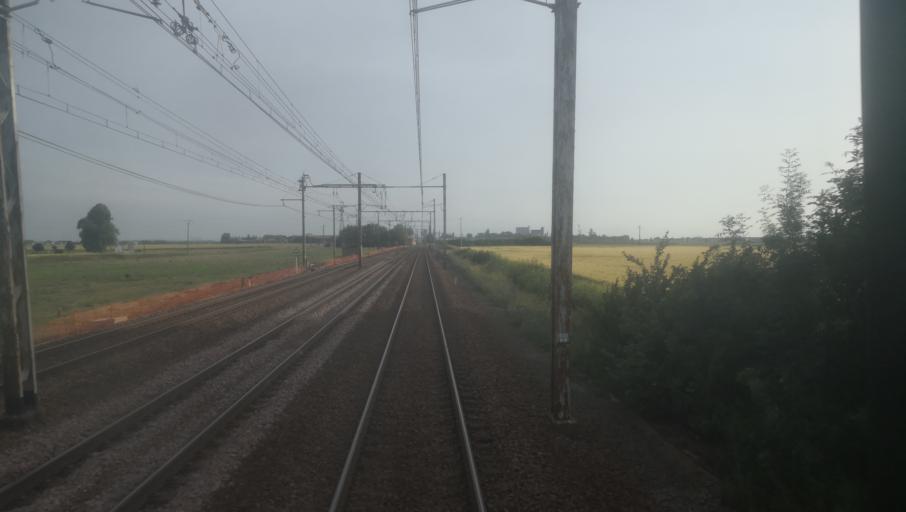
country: FR
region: Centre
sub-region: Departement du Loiret
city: Artenay
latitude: 48.0656
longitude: 1.8788
